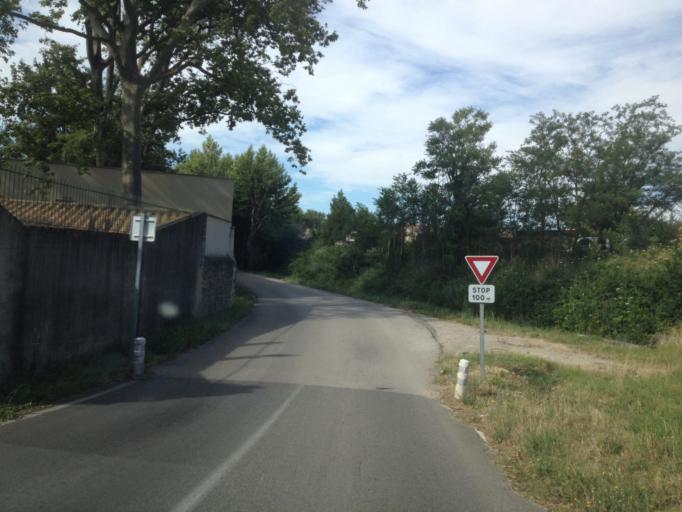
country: FR
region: Provence-Alpes-Cote d'Azur
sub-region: Departement du Vaucluse
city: Sorgues
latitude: 44.0192
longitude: 4.8782
